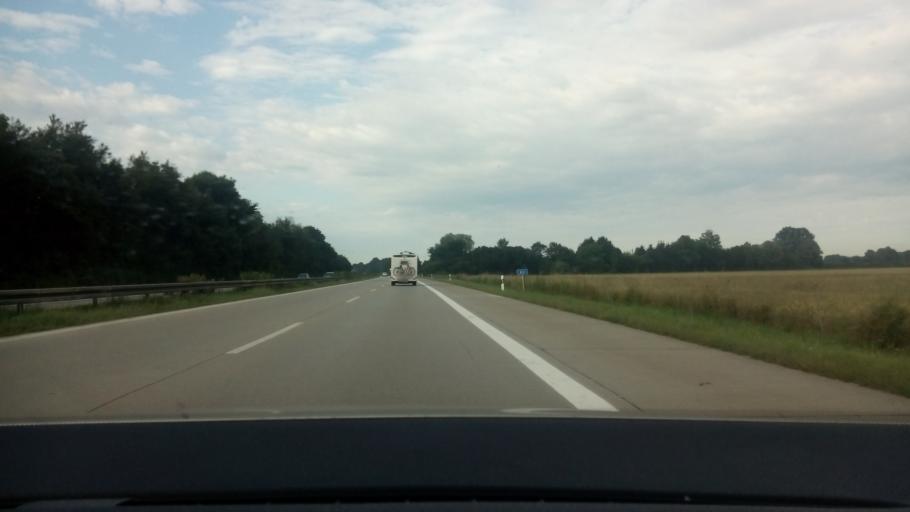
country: DE
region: Bavaria
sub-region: Upper Bavaria
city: Unterschleissheim
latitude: 48.2806
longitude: 11.5516
